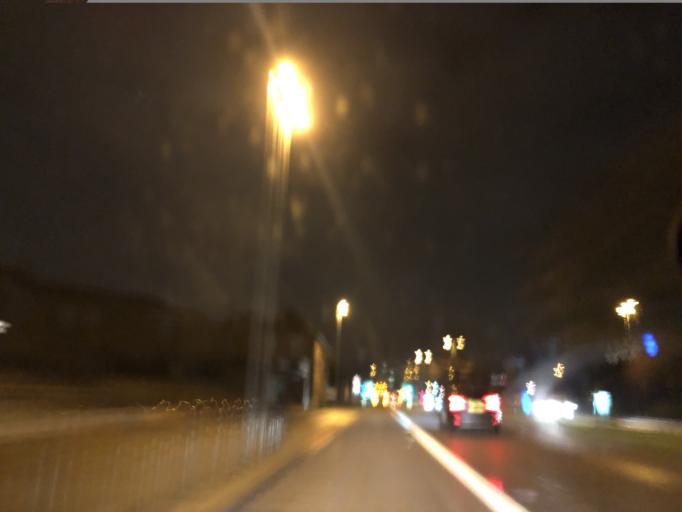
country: GB
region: England
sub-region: Borough of Oldham
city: Oldham
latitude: 53.5346
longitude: -2.1156
